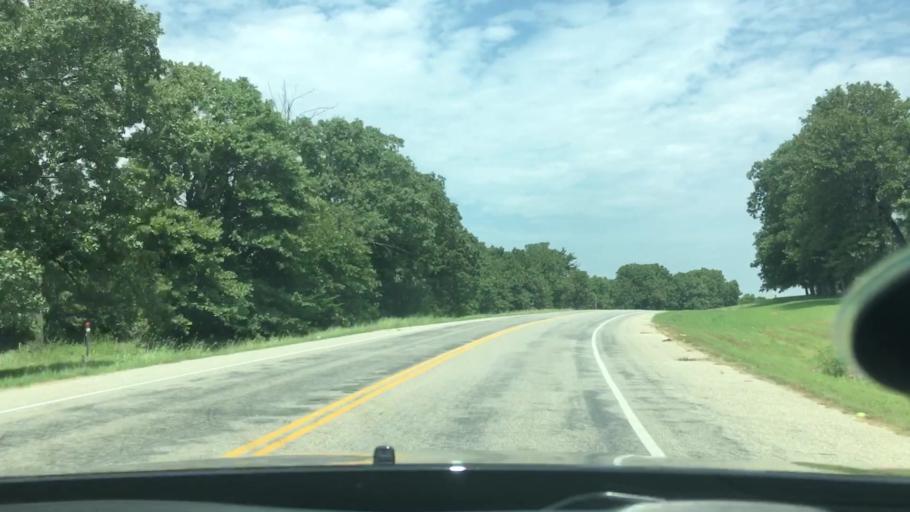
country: US
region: Oklahoma
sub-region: Pontotoc County
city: Byng
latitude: 34.8504
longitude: -96.6785
